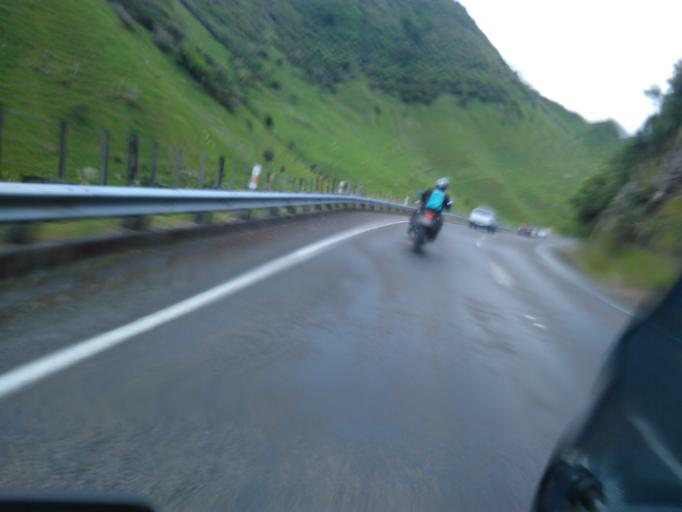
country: NZ
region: Bay of Plenty
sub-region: Opotiki District
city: Opotiki
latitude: -38.3594
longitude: 177.4599
